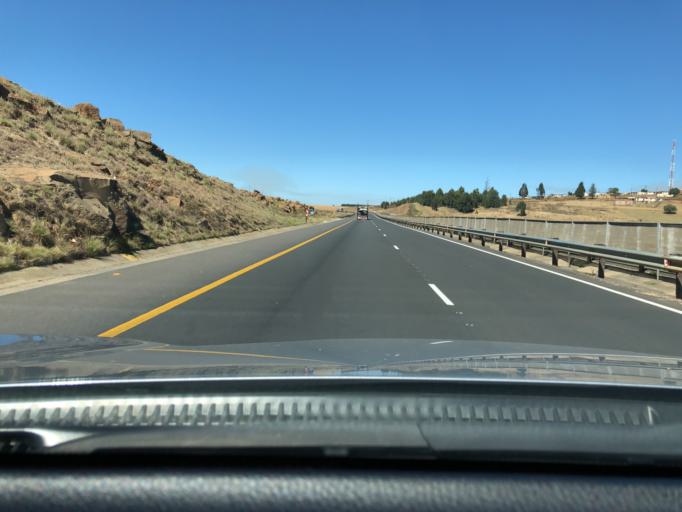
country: ZA
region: KwaZulu-Natal
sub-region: uMgungundlovu District Municipality
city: Mooirivier
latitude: -29.2626
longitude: 30.0219
